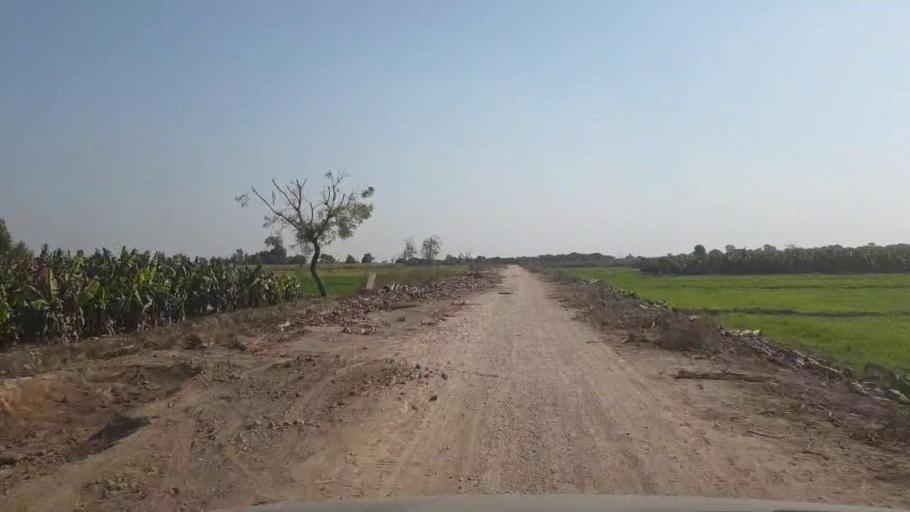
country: PK
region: Sindh
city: Chambar
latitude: 25.3151
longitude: 68.8728
